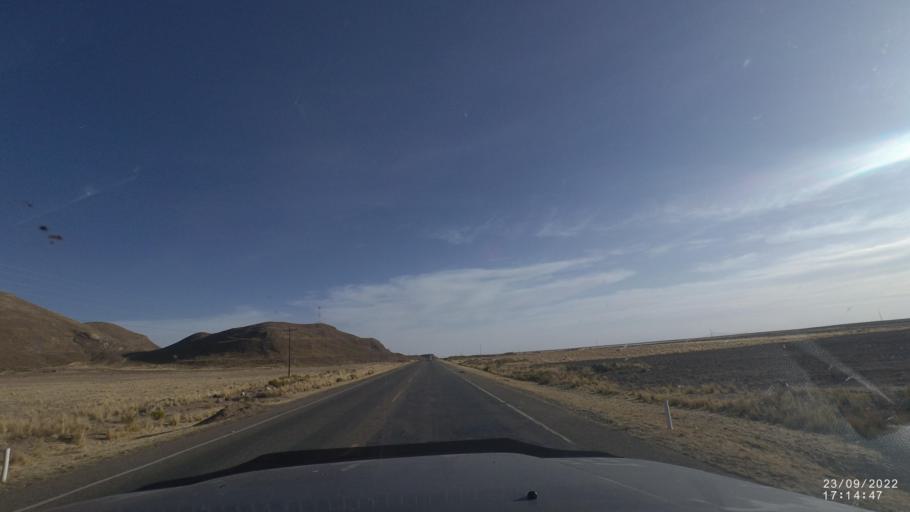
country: BO
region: Oruro
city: Challapata
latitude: -18.7265
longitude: -66.8672
